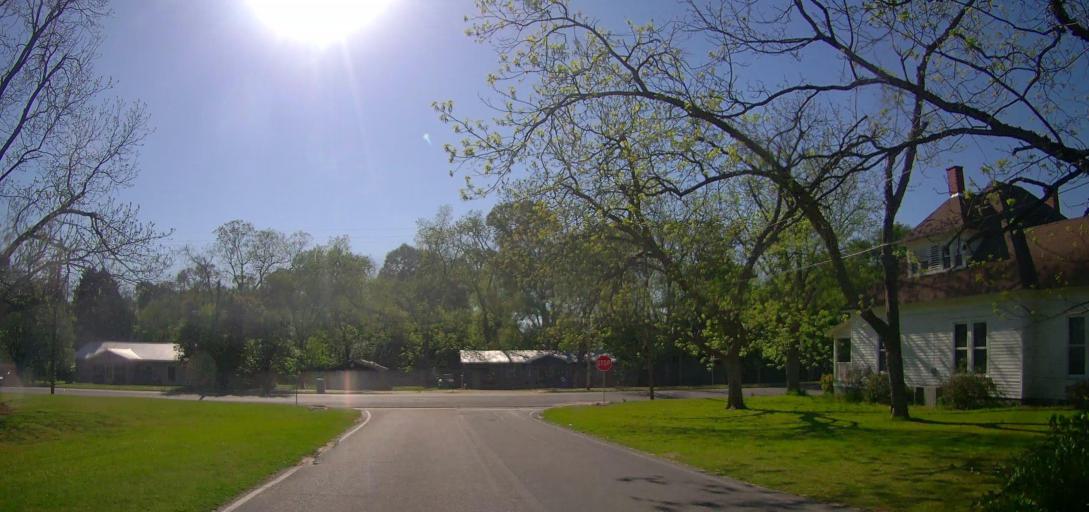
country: US
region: Georgia
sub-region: Wilcox County
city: Rochelle
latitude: 31.9466
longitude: -83.4558
